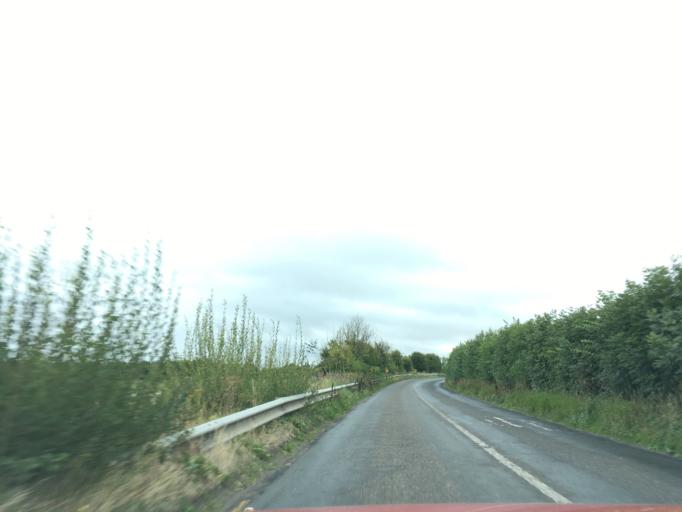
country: IE
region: Munster
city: Cashel
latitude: 52.4526
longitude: -7.8150
